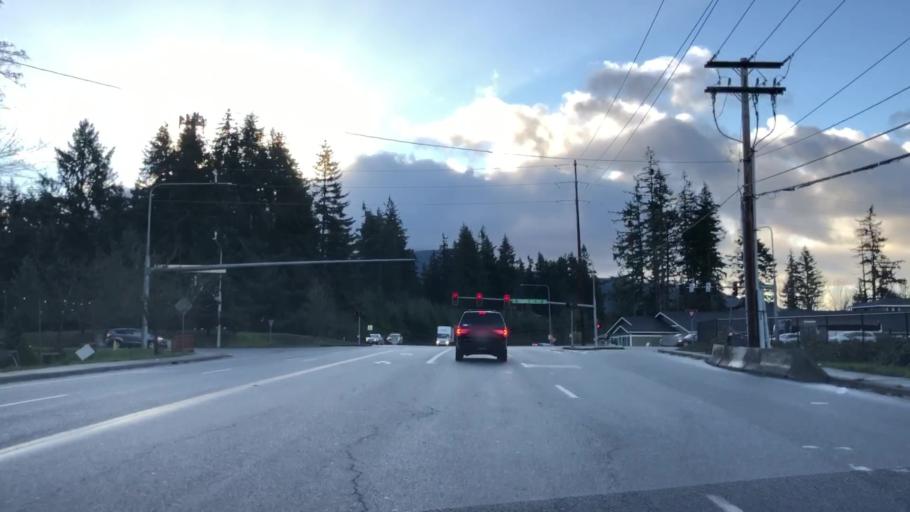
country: US
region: Washington
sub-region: King County
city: Issaquah
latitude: 47.5554
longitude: -122.0220
